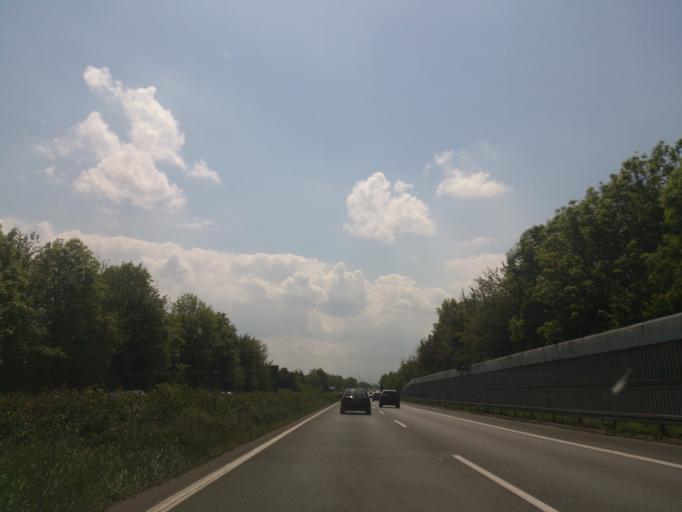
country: DE
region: North Rhine-Westphalia
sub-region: Regierungsbezirk Detmold
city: Paderborn
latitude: 51.7257
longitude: 8.7060
